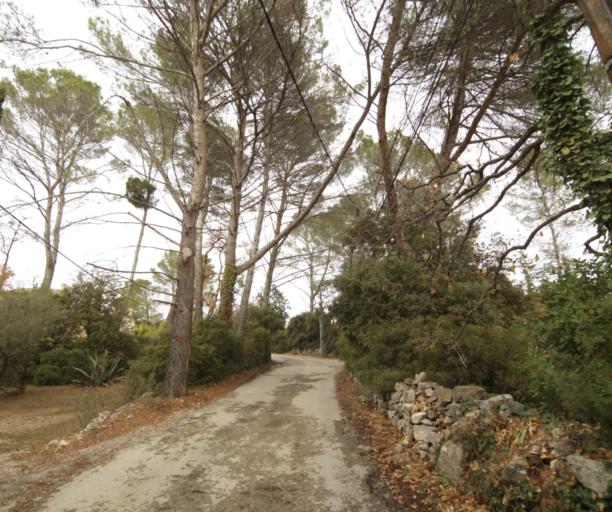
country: FR
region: Provence-Alpes-Cote d'Azur
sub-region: Departement du Var
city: Trans-en-Provence
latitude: 43.5088
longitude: 6.4909
